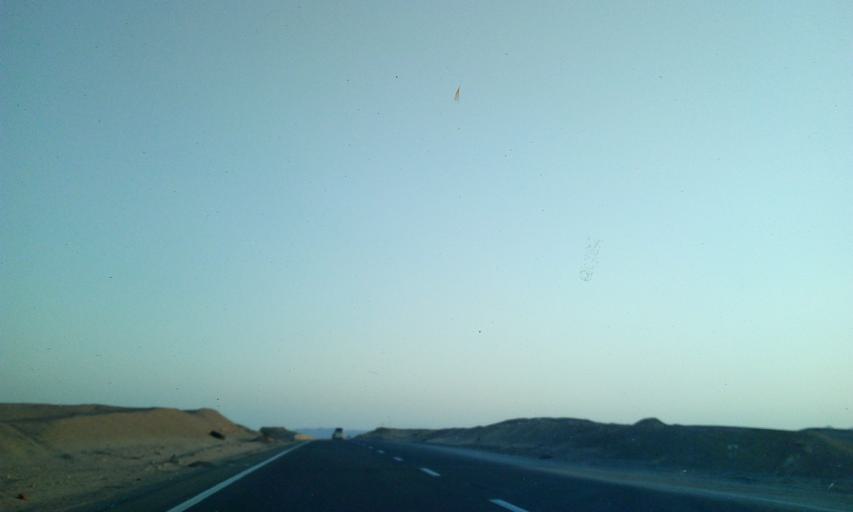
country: EG
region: Red Sea
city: El Gouna
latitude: 27.7309
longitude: 33.5075
